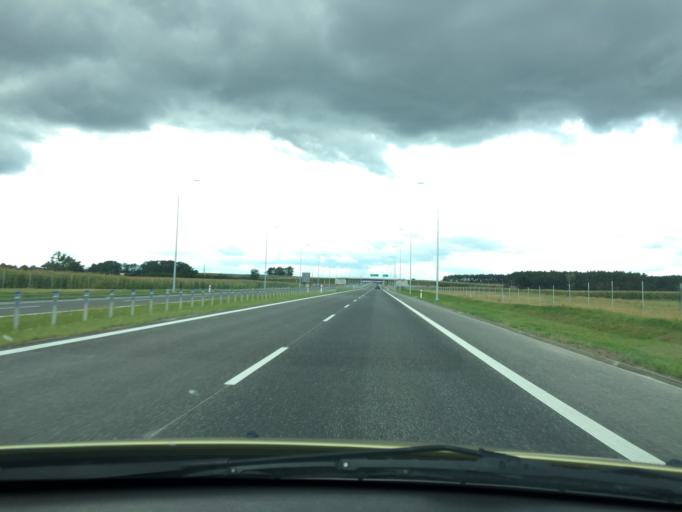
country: PL
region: Greater Poland Voivodeship
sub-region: Powiat jarocinski
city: Jarocin
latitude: 52.0301
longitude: 17.4724
